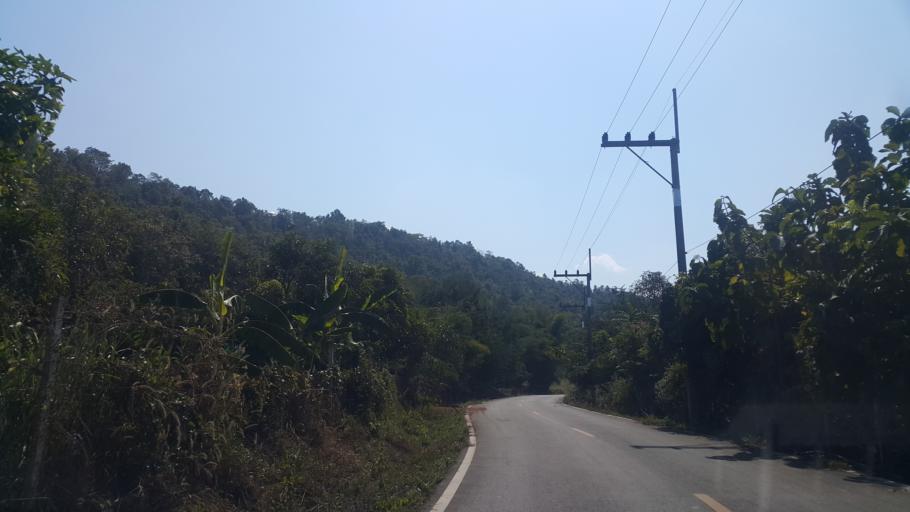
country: TH
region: Chiang Mai
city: San Kamphaeng
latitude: 18.6905
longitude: 99.1692
